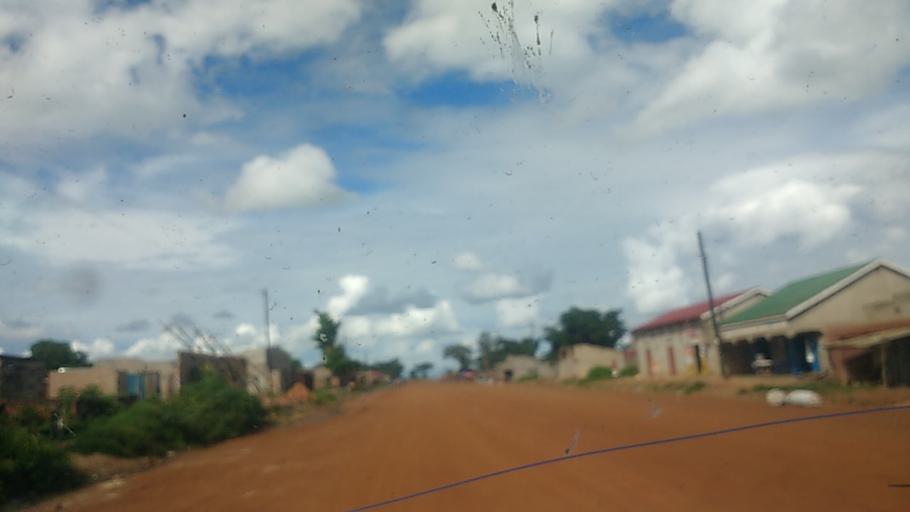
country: UG
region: Eastern Region
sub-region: Katakwi District
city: Katakwi
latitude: 1.9197
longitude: 33.9855
